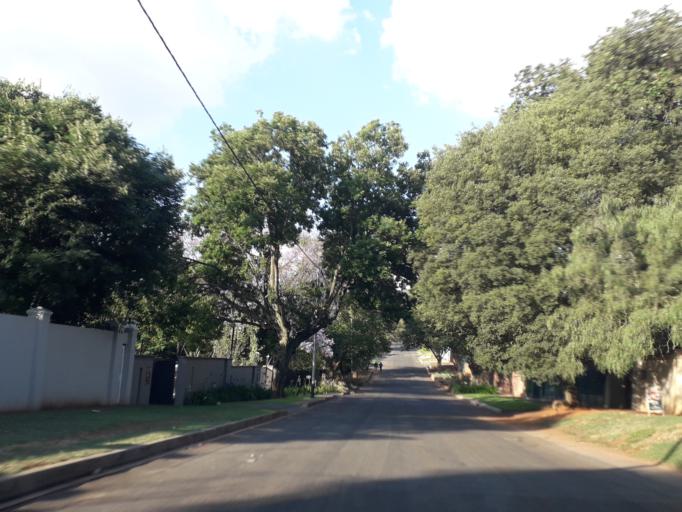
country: ZA
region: Gauteng
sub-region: City of Johannesburg Metropolitan Municipality
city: Johannesburg
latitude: -26.1334
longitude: 27.9918
